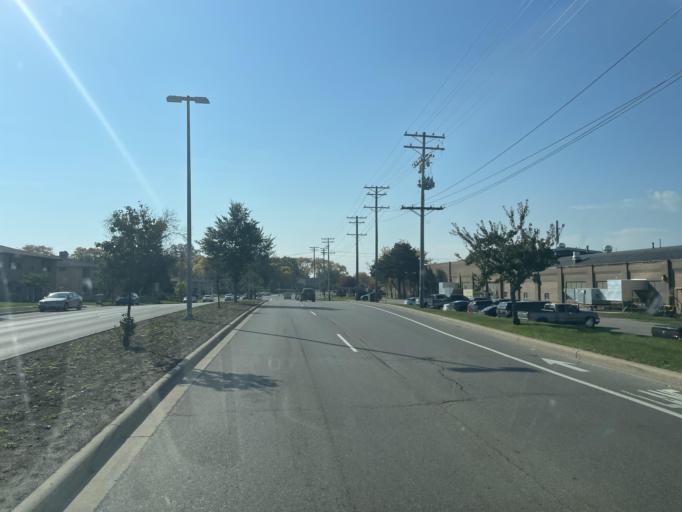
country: US
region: Wisconsin
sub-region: Dane County
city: Madison
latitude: 43.0403
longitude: -89.4040
